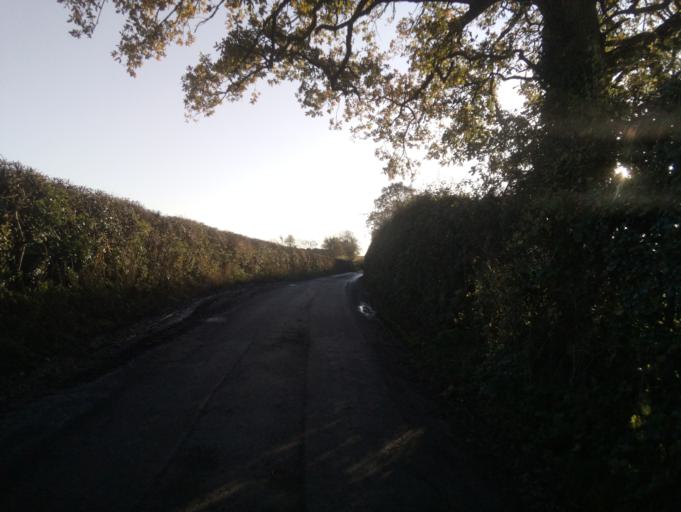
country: GB
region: England
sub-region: Somerset
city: Milborne Port
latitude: 50.9940
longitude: -2.4589
